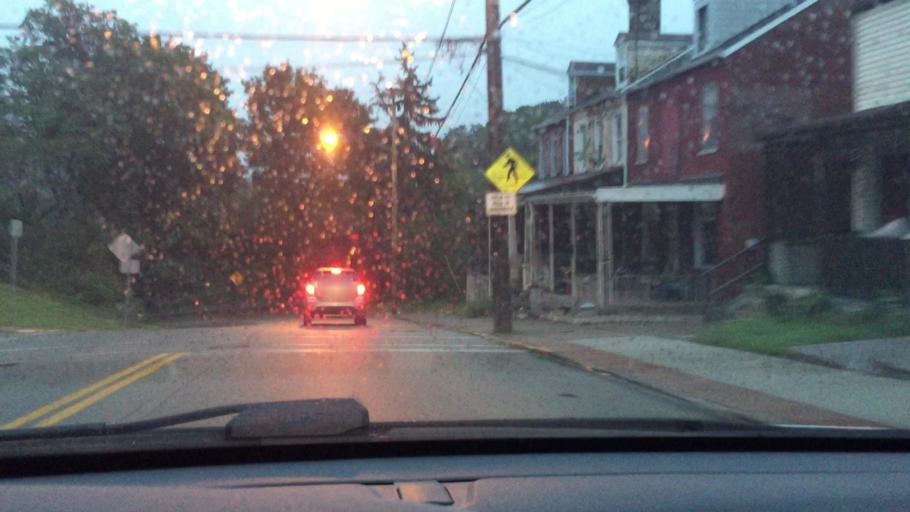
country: US
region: Pennsylvania
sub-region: Allegheny County
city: Crafton
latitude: 40.4415
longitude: -80.0406
